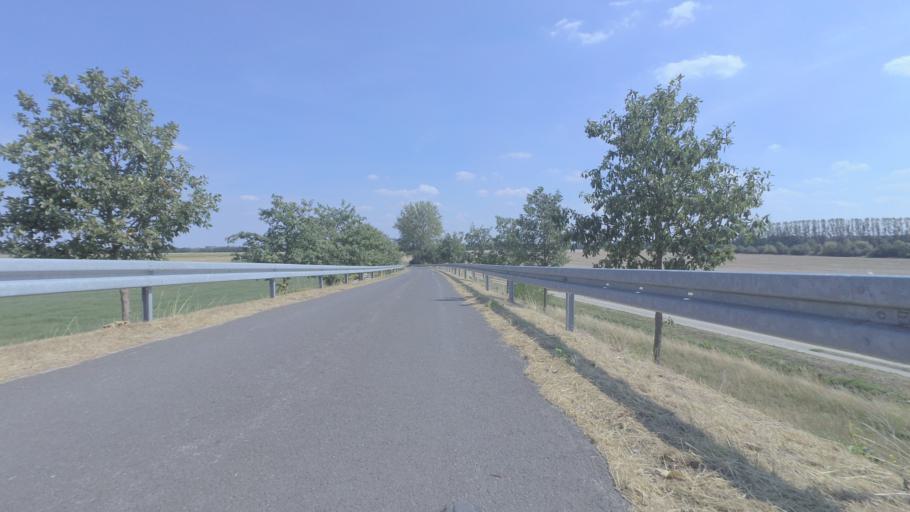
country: DE
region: Brandenburg
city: Trebbin
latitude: 52.1767
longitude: 13.2478
